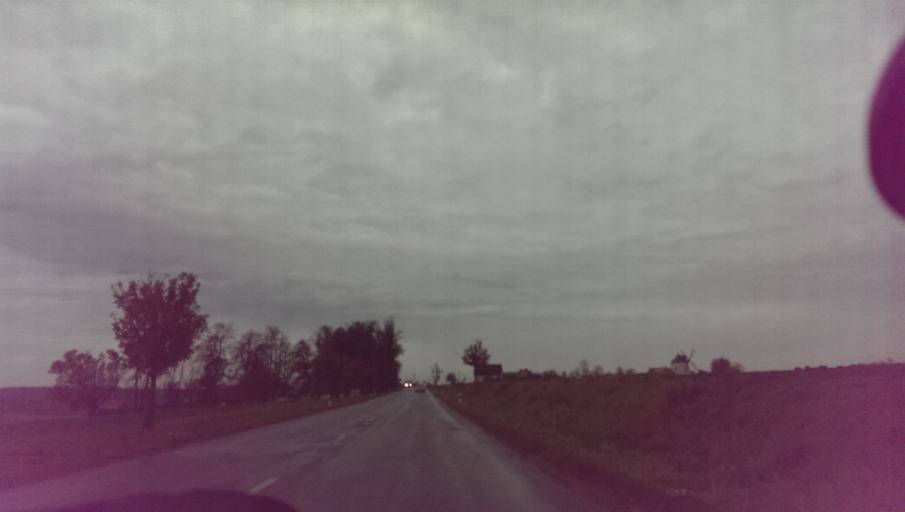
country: AT
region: Lower Austria
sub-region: Politischer Bezirk Hollabrunn
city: Hardegg
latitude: 48.9048
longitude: 15.8781
